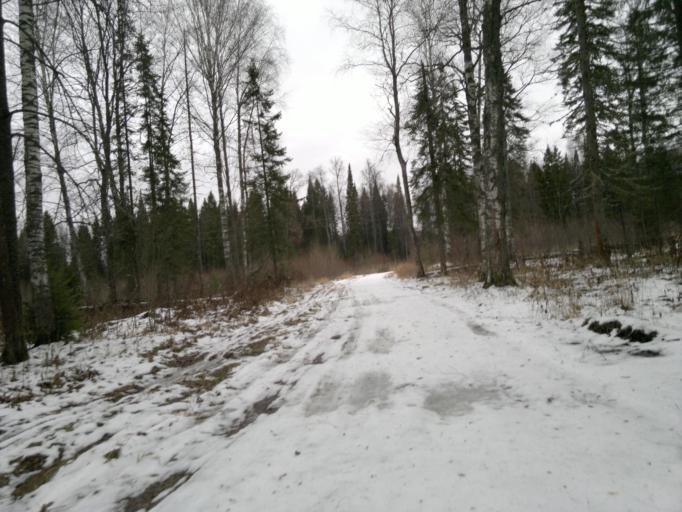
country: RU
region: Mariy-El
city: Yoshkar-Ola
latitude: 56.5946
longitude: 47.9679
